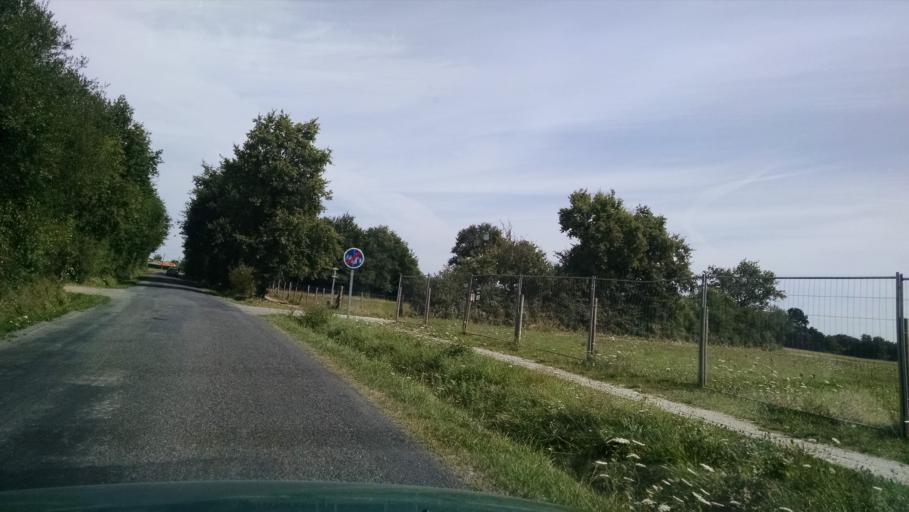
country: FR
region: Pays de la Loire
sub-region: Departement de la Loire-Atlantique
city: Clisson
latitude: 47.1005
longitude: -1.2760
